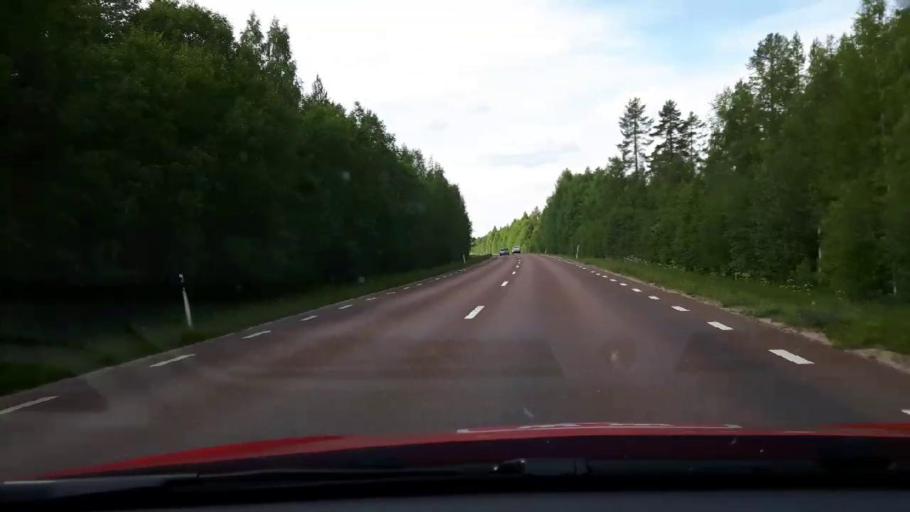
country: SE
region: Jaemtland
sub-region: Harjedalens Kommun
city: Sveg
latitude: 62.0466
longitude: 14.8381
